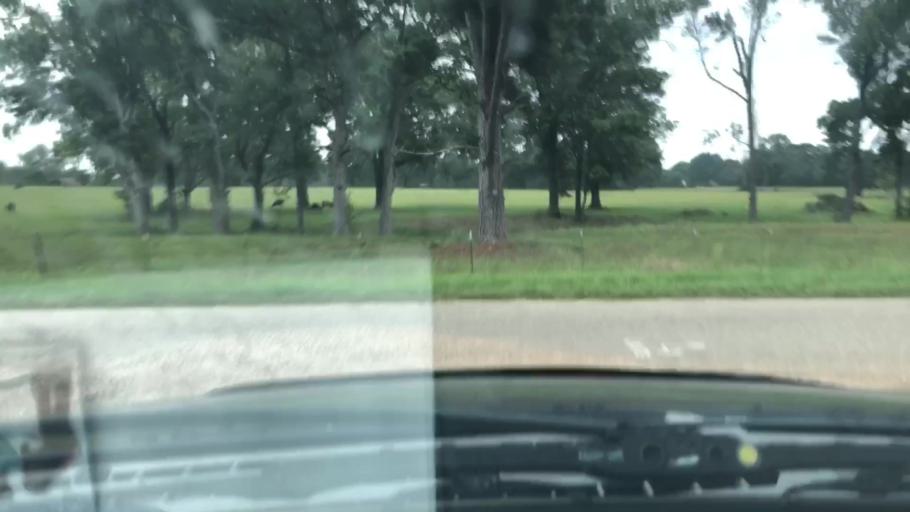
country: US
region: Texas
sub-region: Bowie County
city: Wake Village
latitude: 33.3759
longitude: -94.0955
